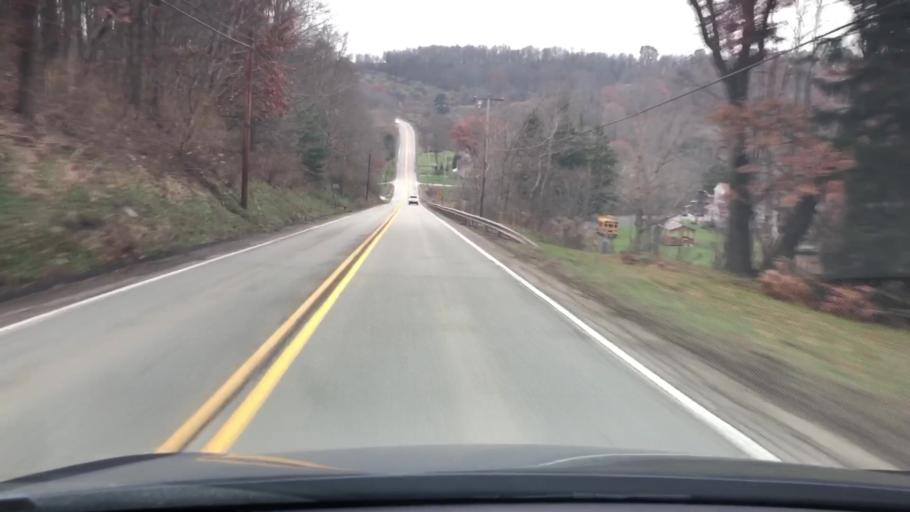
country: US
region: Pennsylvania
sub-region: Armstrong County
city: Kittanning
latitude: 40.8482
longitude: -79.4600
